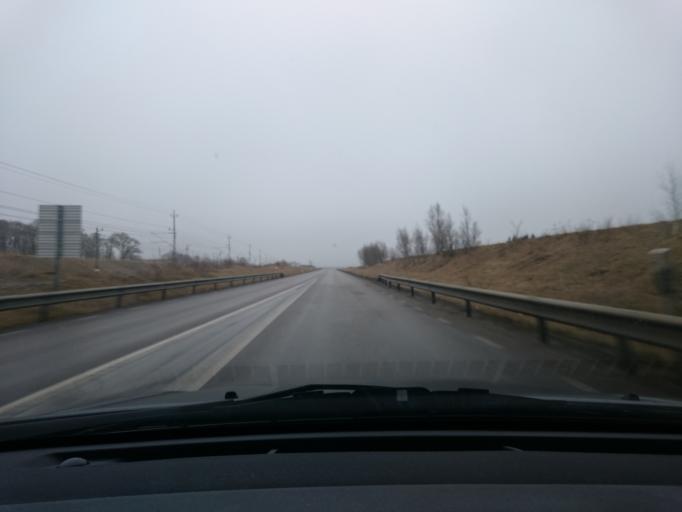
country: SE
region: Skane
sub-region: Bastads Kommun
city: Forslov
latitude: 56.3438
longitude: 12.8013
